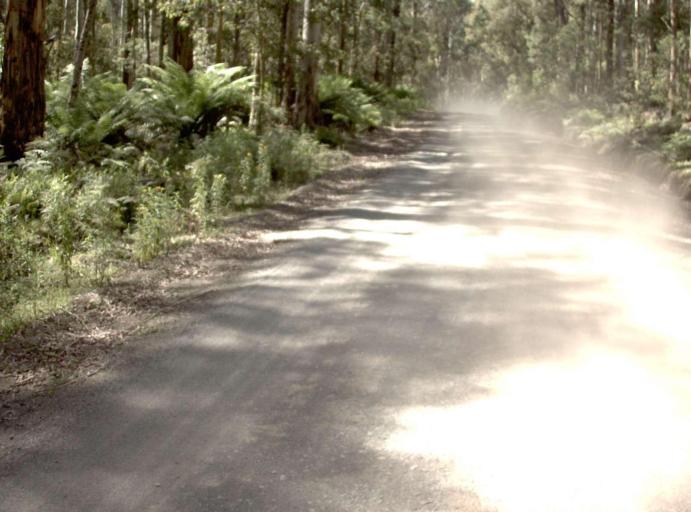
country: AU
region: New South Wales
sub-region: Bombala
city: Bombala
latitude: -37.2370
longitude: 148.7554
